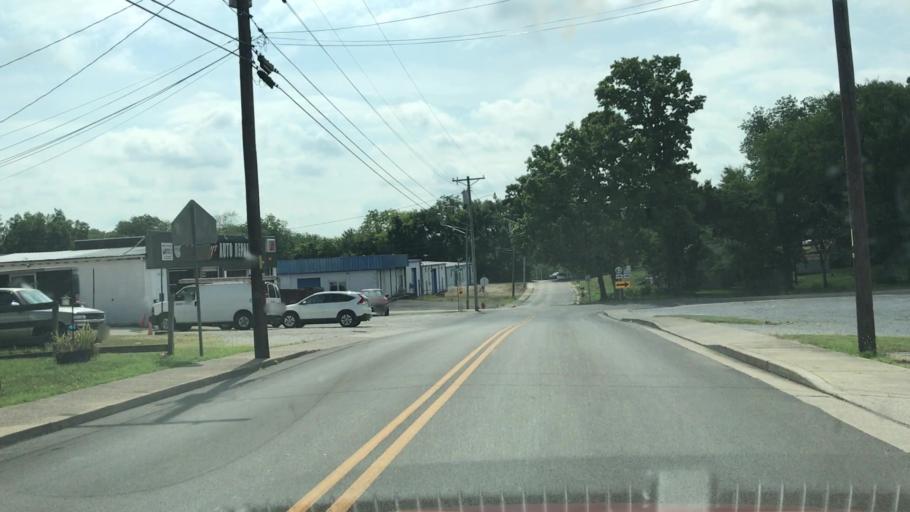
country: US
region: Kentucky
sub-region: Barren County
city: Glasgow
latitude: 36.9919
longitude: -85.9099
